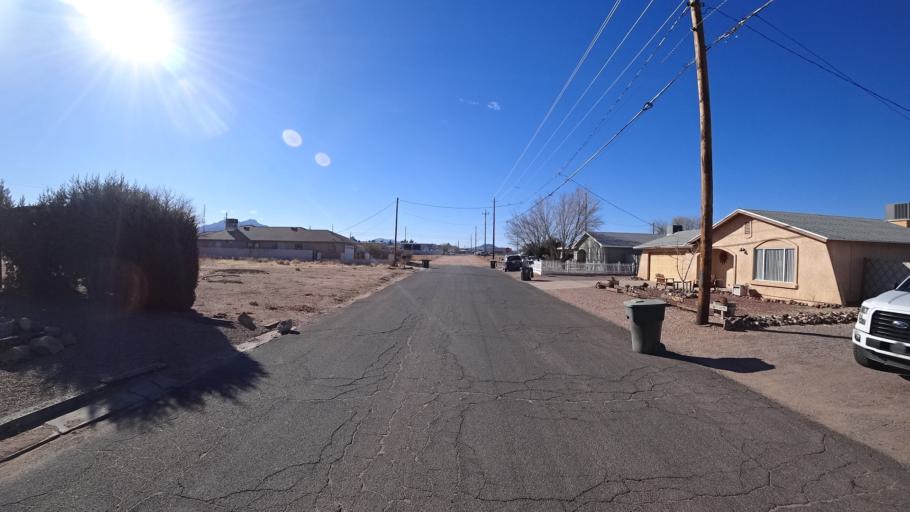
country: US
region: Arizona
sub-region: Mohave County
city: New Kingman-Butler
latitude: 35.2272
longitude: -114.0149
